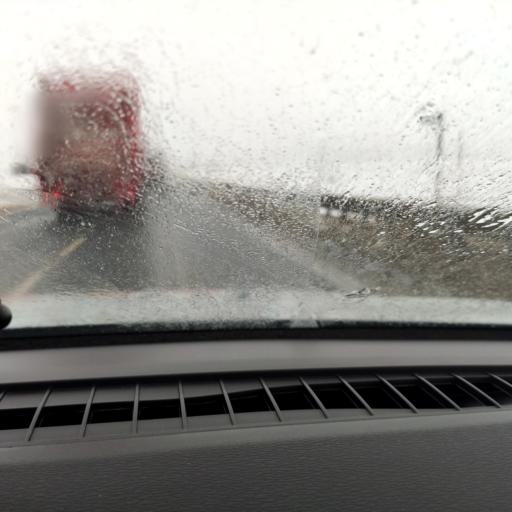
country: RU
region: Saratov
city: Perelyub
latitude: 52.1565
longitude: 50.8048
